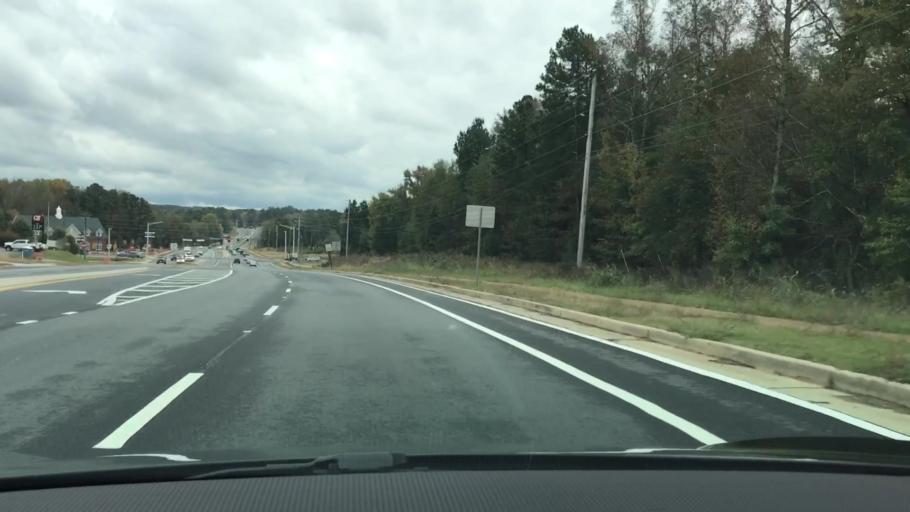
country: US
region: Georgia
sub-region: Oconee County
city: Watkinsville
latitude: 33.9092
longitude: -83.4654
